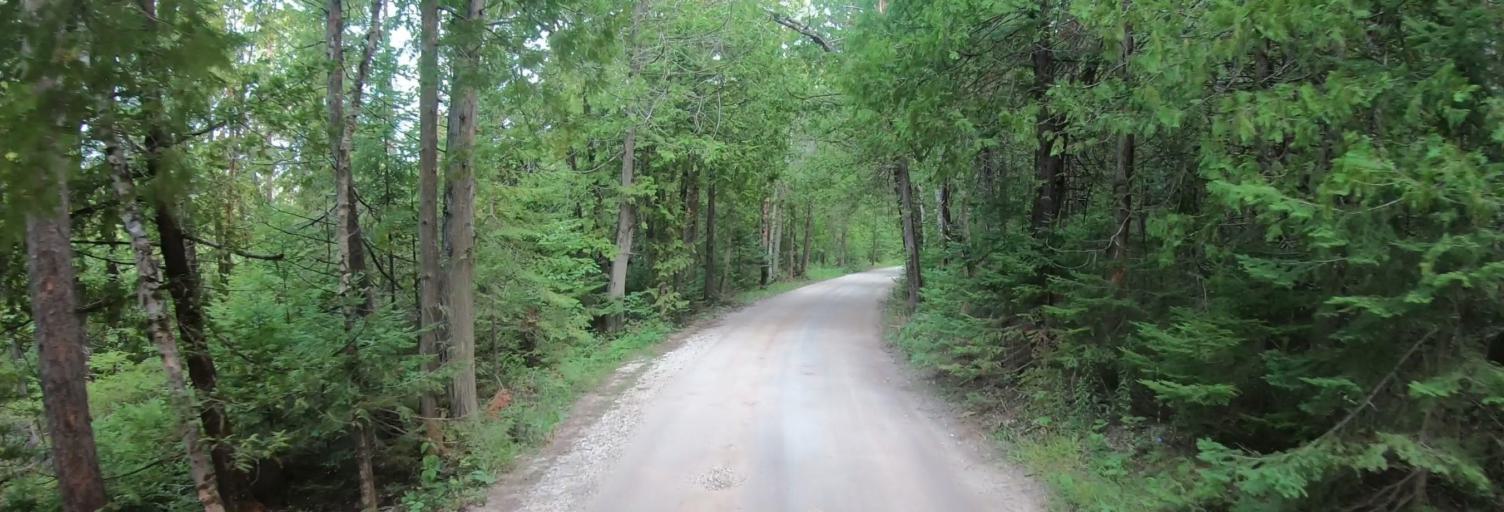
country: US
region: Michigan
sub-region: Mackinac County
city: Saint Ignace
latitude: 45.7659
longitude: -84.7717
